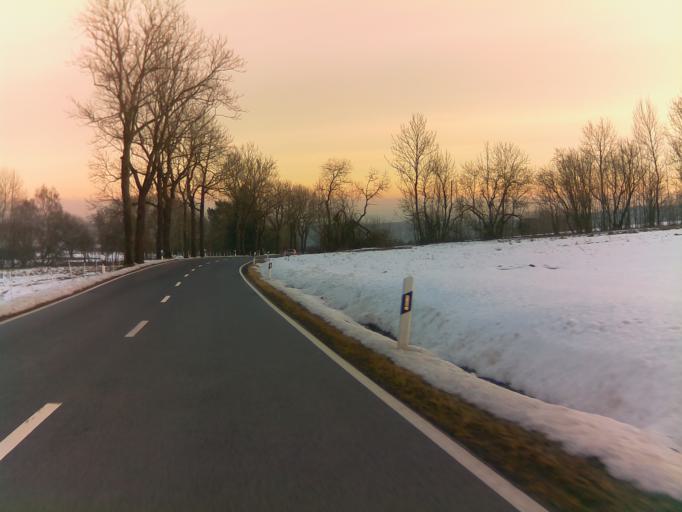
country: DE
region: Bavaria
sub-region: Regierungsbezirk Unterfranken
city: Bischofsheim an der Rhon
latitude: 50.4220
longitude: 9.9912
